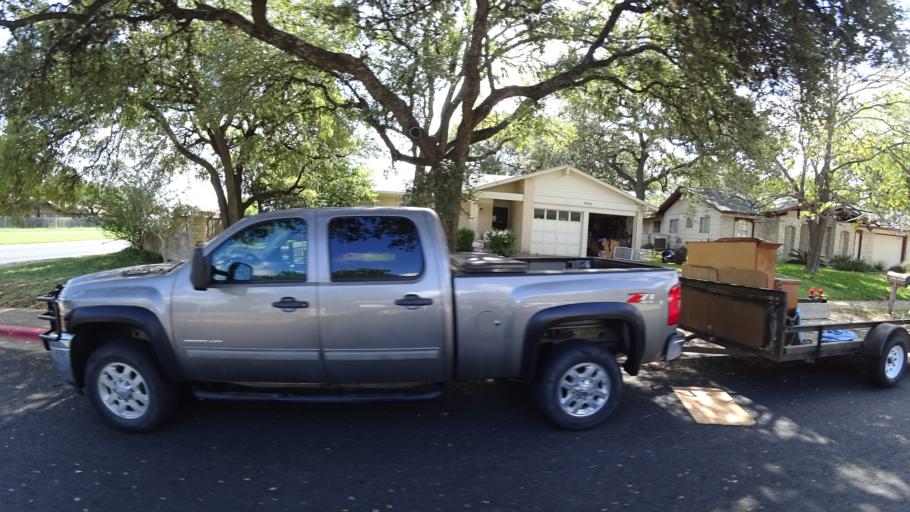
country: US
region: Texas
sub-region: Travis County
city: Shady Hollow
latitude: 30.2040
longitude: -97.8100
